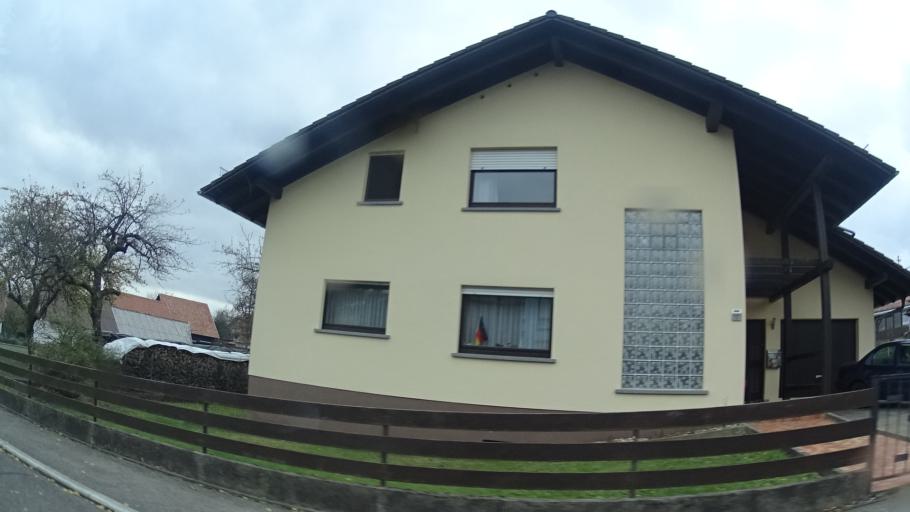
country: DE
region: Baden-Wuerttemberg
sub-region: Karlsruhe Region
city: Neckargerach
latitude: 49.4362
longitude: 9.0761
